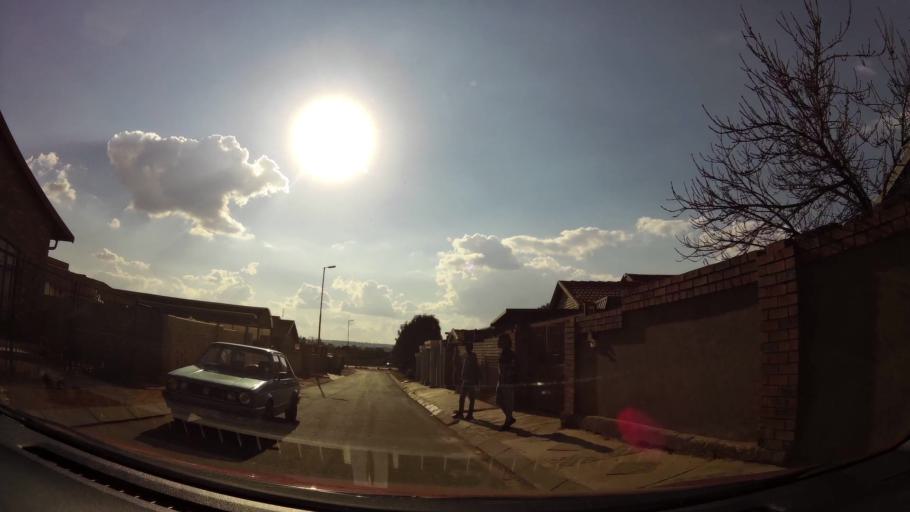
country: ZA
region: Gauteng
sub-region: City of Johannesburg Metropolitan Municipality
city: Soweto
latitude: -26.2297
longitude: 27.8700
